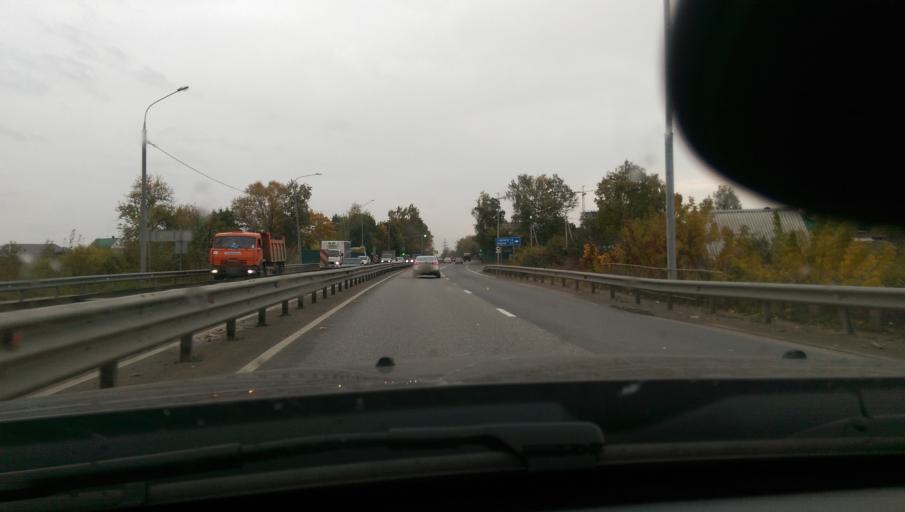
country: RU
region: Moscow
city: Vatutino
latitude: 55.9267
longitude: 37.6607
